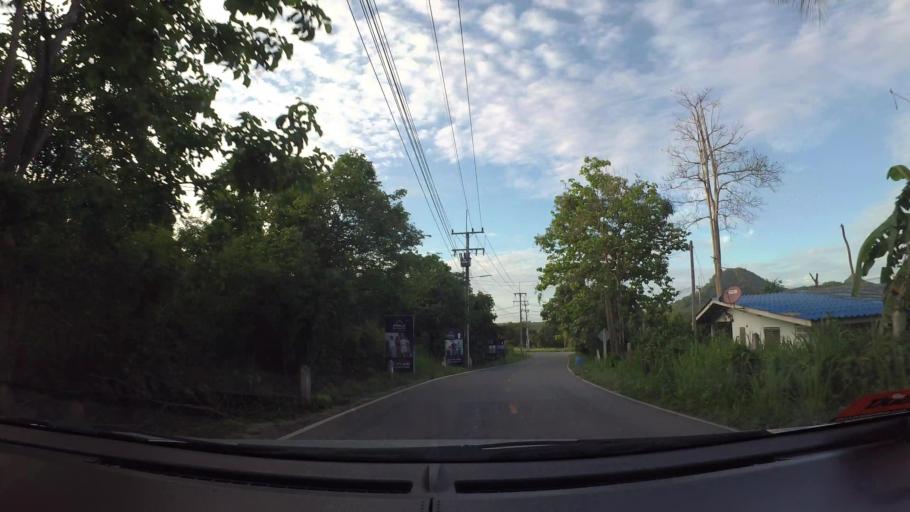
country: TH
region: Chon Buri
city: Sattahip
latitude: 12.7481
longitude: 100.9329
